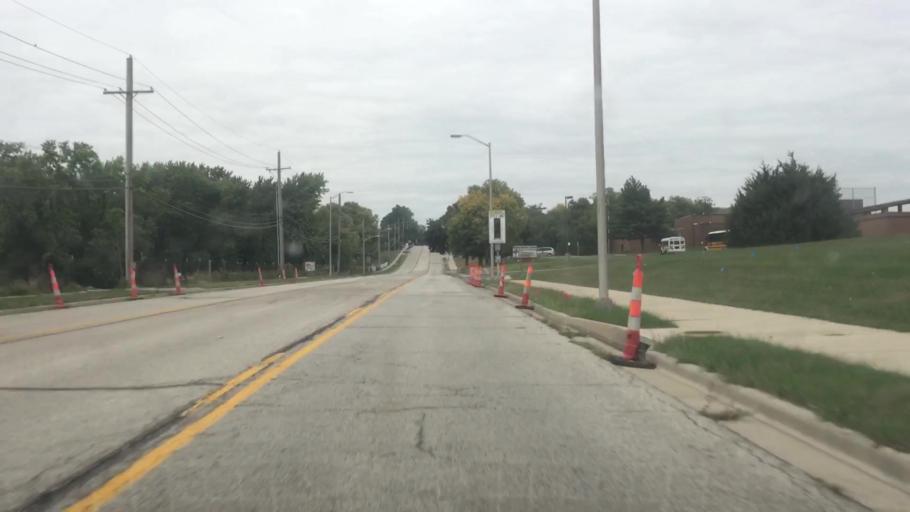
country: US
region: Kansas
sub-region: Johnson County
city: Lenexa
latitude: 39.0012
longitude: -94.7705
